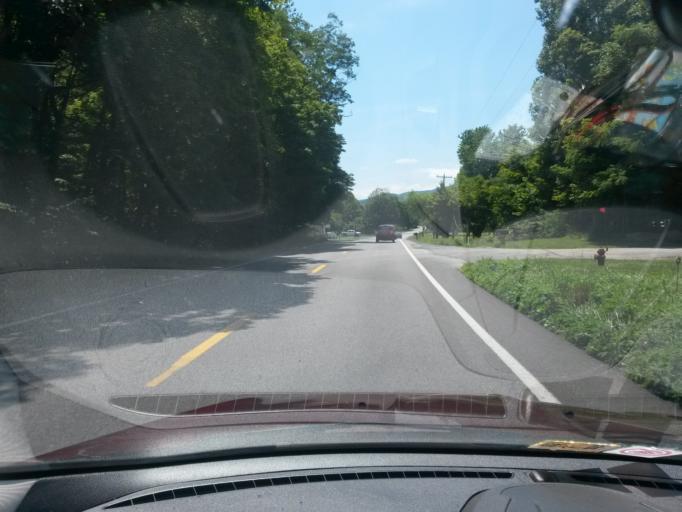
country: US
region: West Virginia
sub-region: Mineral County
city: Keyser
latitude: 39.3450
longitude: -79.0609
